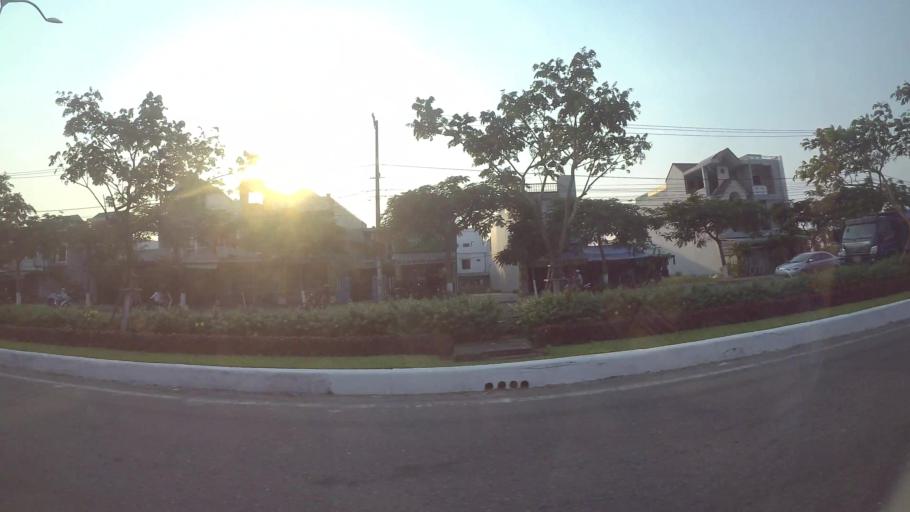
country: VN
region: Da Nang
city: Ngu Hanh Son
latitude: 15.9908
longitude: 108.2578
